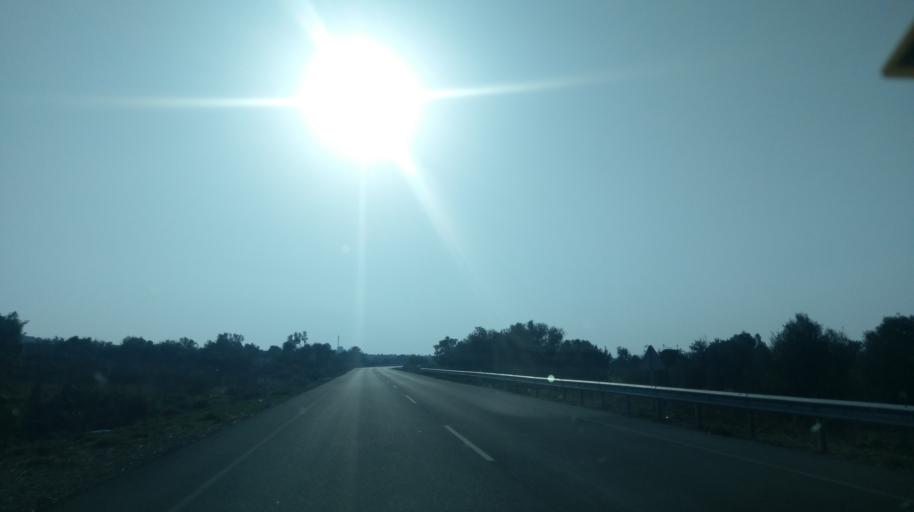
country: CY
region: Ammochostos
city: Leonarisso
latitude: 35.5514
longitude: 34.2098
